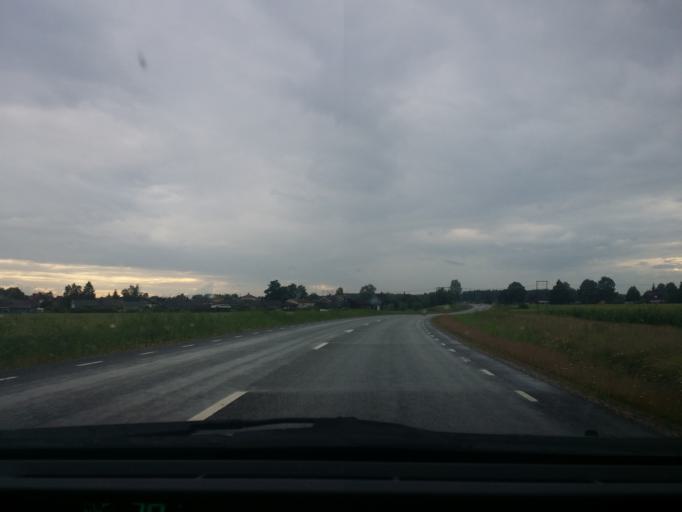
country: SE
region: Vaestmanland
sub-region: Arboga Kommun
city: Arboga
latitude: 59.4031
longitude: 15.8606
